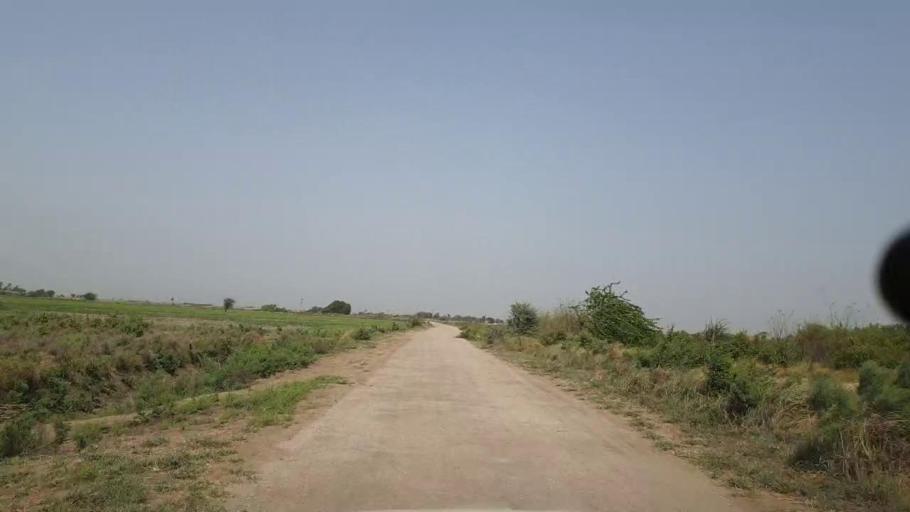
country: PK
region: Sindh
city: Matli
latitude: 25.0701
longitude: 68.6899
